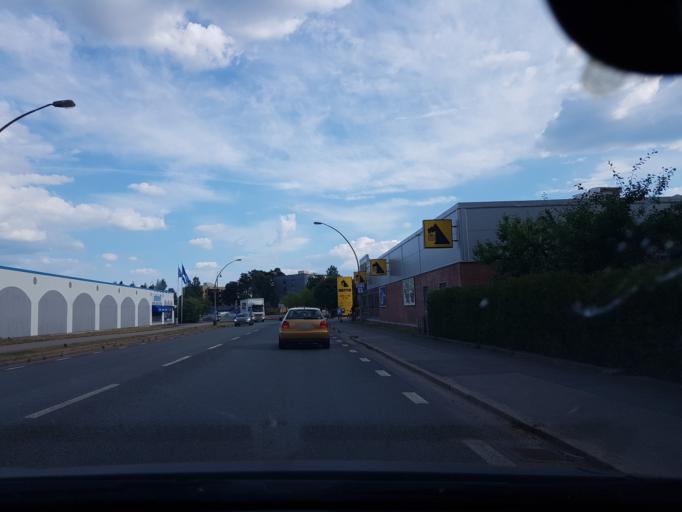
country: SE
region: Joenkoeping
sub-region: Gislaveds Kommun
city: Gislaved
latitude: 57.3027
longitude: 13.5436
